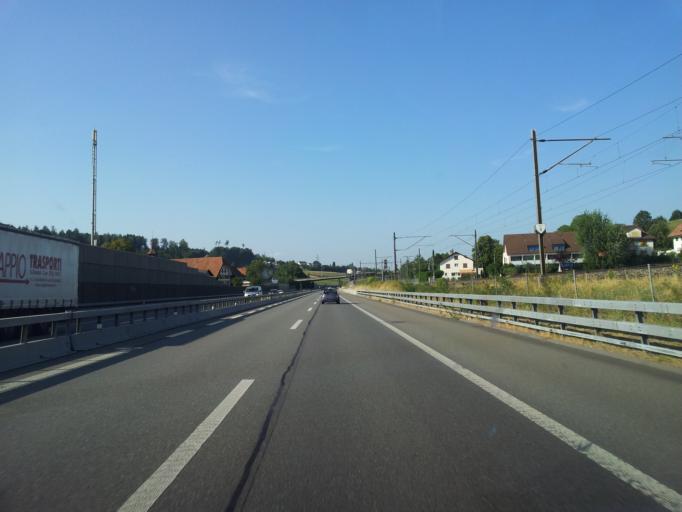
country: CH
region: Fribourg
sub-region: Sense District
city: Flamatt
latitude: 46.9123
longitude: 7.3609
